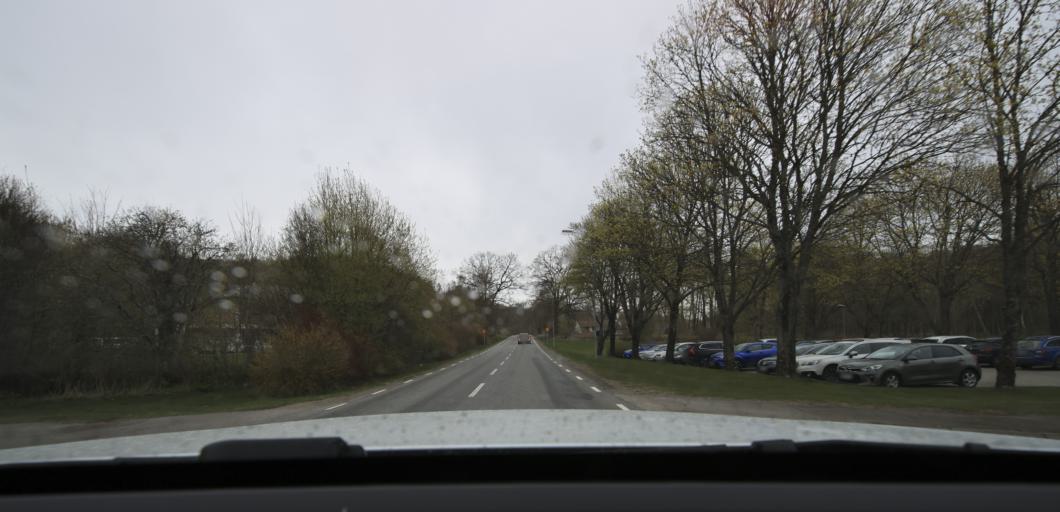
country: SE
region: Halland
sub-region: Varbergs Kommun
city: Tvaaker
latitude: 57.1458
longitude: 12.4602
